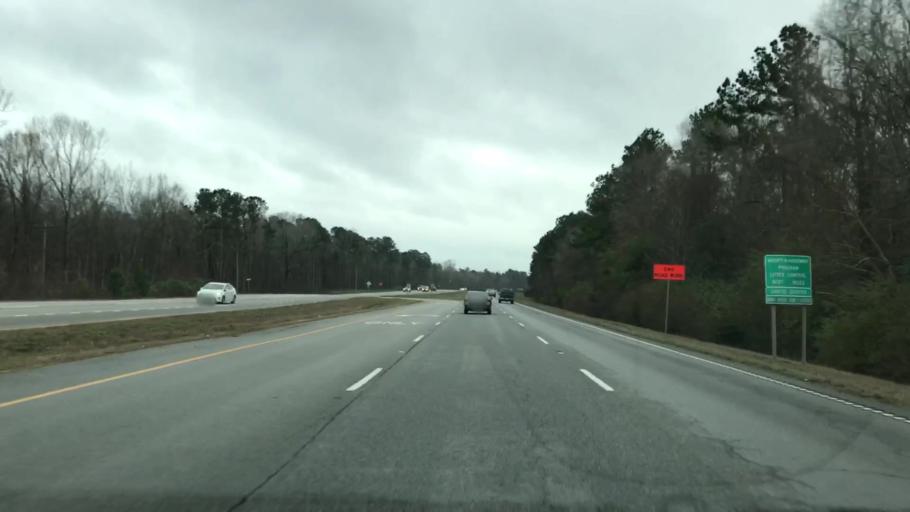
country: US
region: South Carolina
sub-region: Berkeley County
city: Moncks Corner
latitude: 33.1247
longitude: -80.0293
